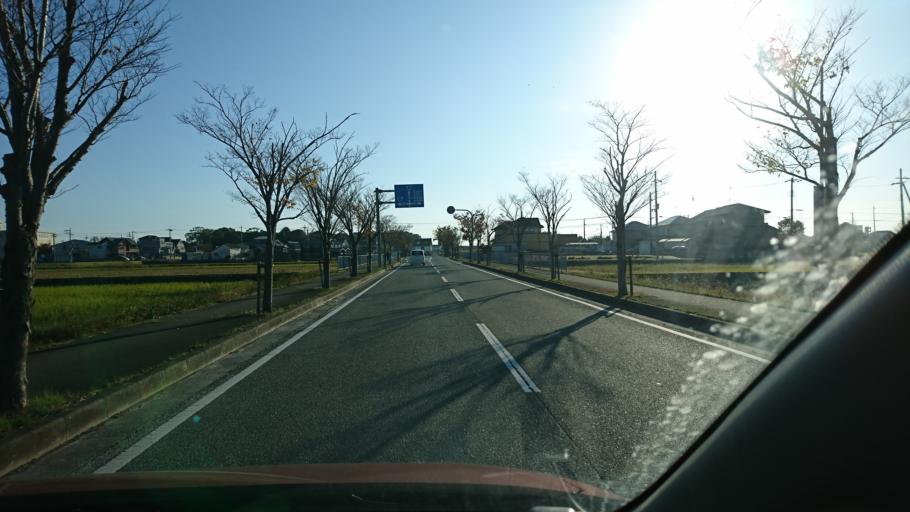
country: JP
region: Hyogo
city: Miki
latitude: 34.7661
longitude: 134.9159
